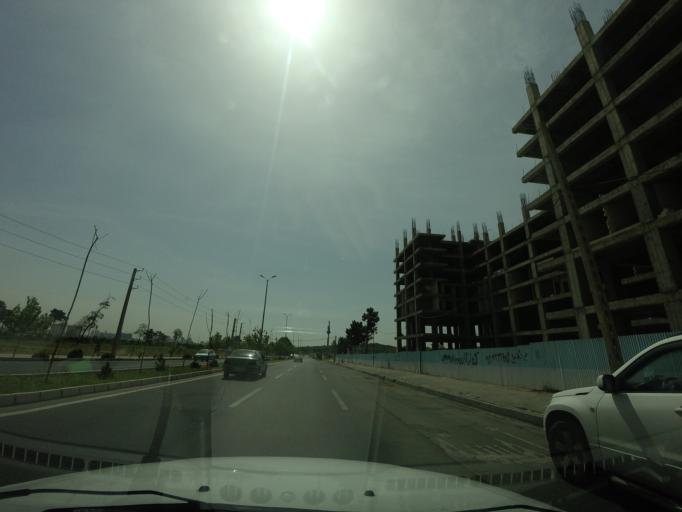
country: IR
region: Tehran
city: Shahr-e Qods
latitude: 35.7520
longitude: 51.1986
